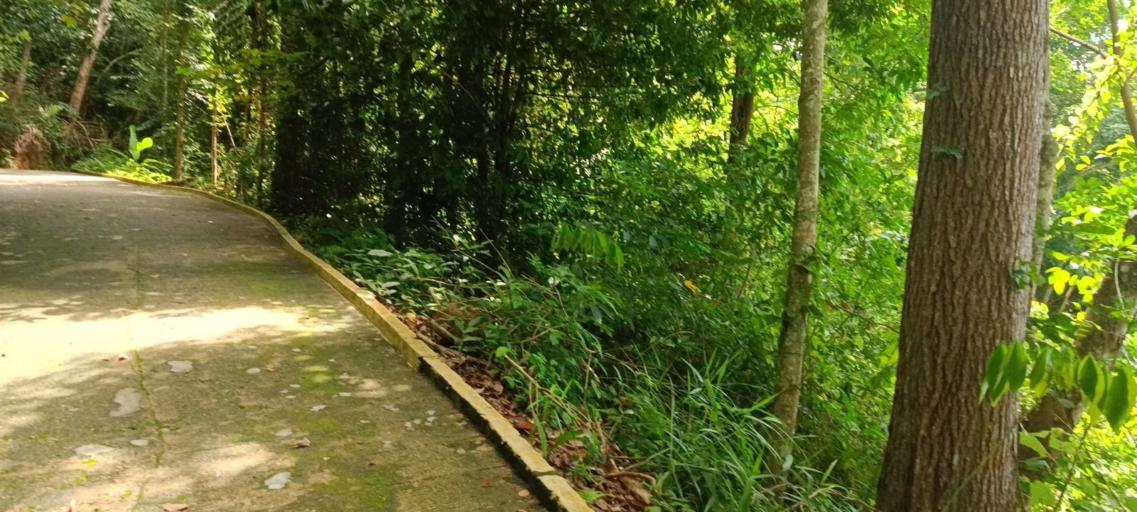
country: MY
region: Penang
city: Kampung Sungai Ara
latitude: 5.3228
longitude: 100.2438
